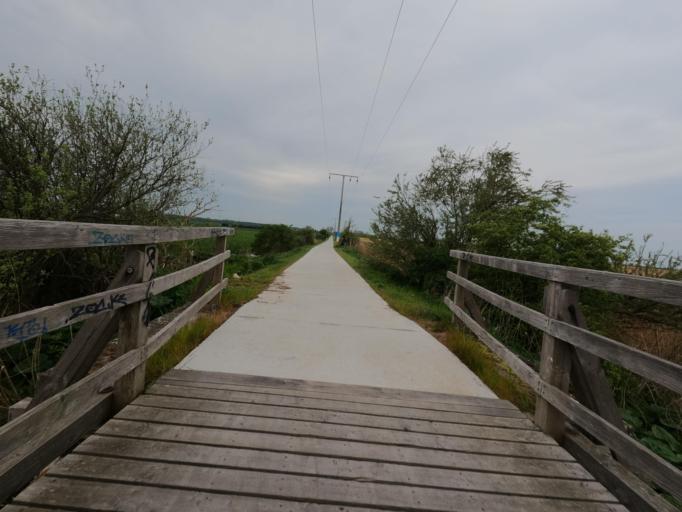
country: DE
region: Mecklenburg-Vorpommern
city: Saal
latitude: 54.3058
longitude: 12.5008
